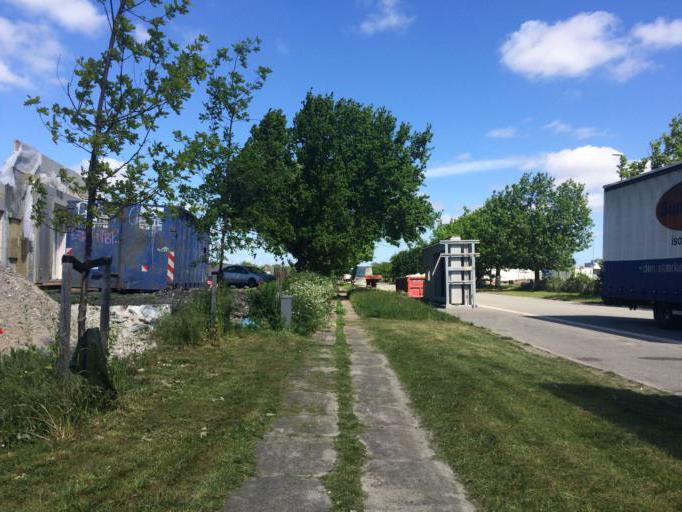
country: DK
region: Capital Region
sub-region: Hvidovre Kommune
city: Hvidovre
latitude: 55.6093
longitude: 12.4595
